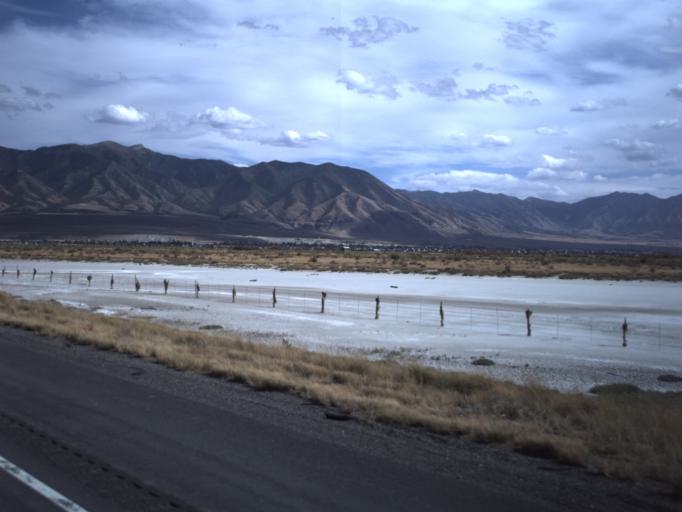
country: US
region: Utah
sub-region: Tooele County
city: Stansbury park
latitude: 40.6622
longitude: -112.3375
